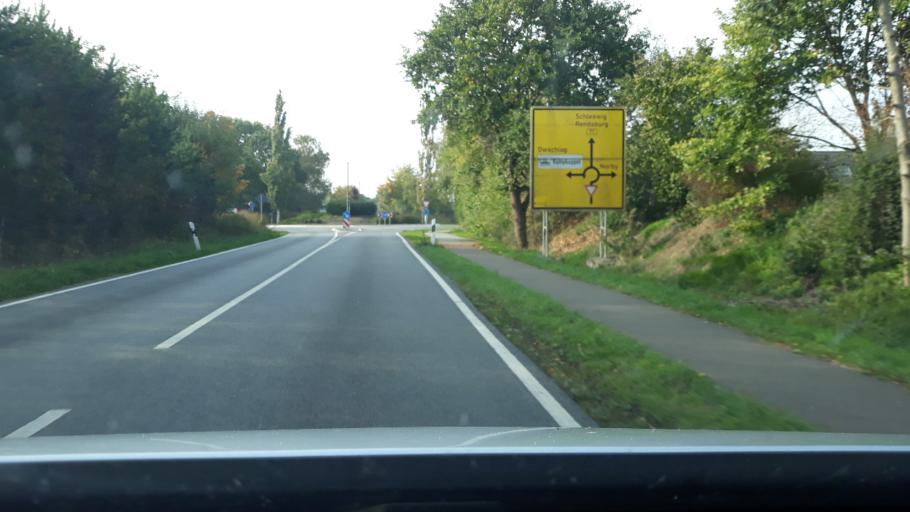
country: DE
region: Schleswig-Holstein
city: Owschlag
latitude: 54.3962
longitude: 9.5746
